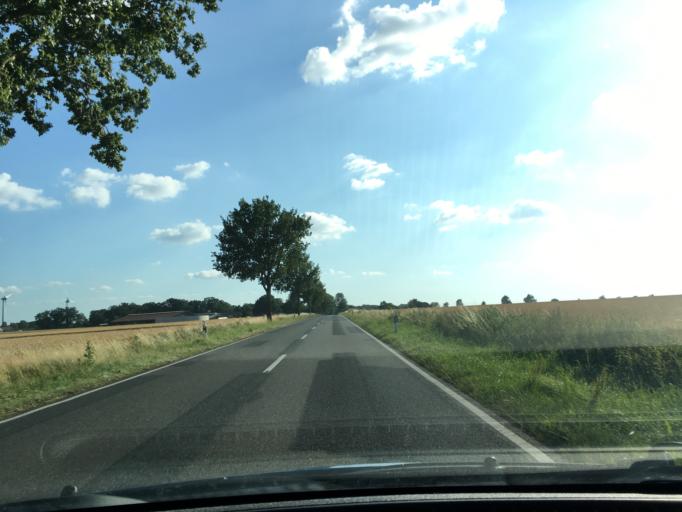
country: DE
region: Lower Saxony
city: Altenmedingen
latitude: 53.1406
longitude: 10.6416
